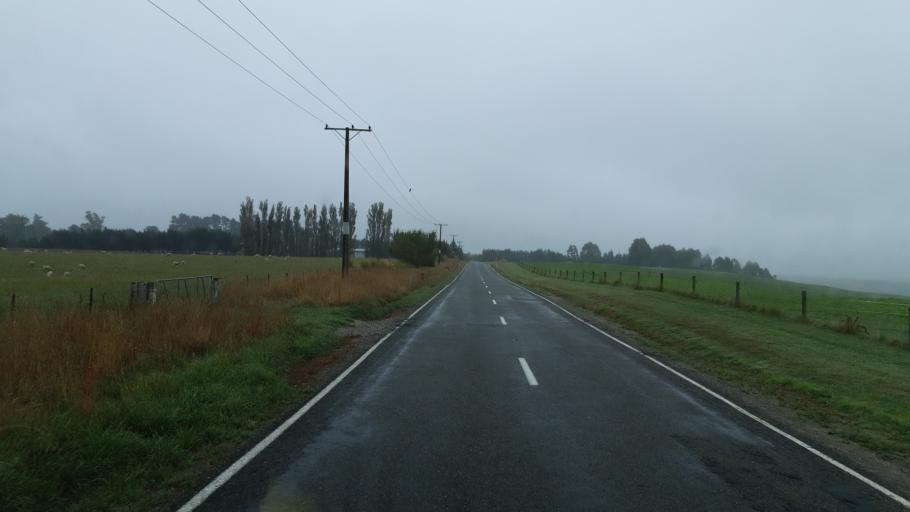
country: NZ
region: Otago
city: Oamaru
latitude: -44.9285
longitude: 170.7972
